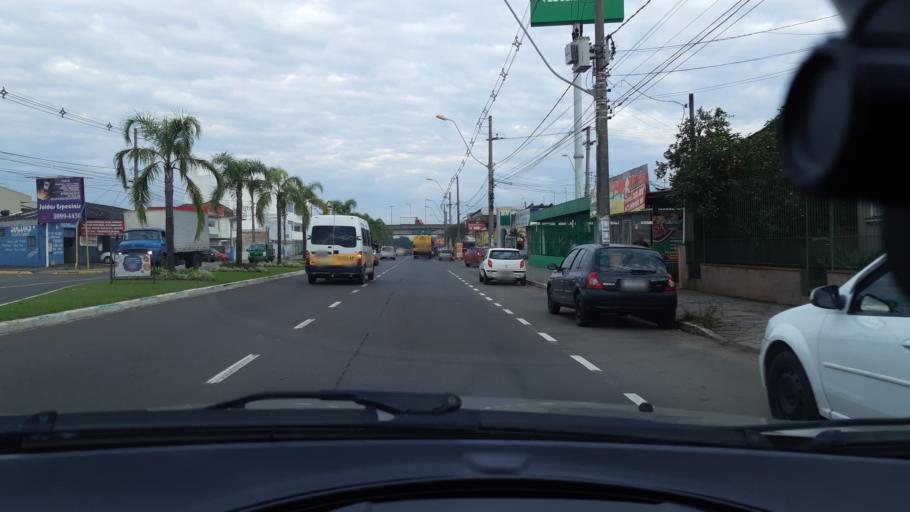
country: BR
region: Rio Grande do Sul
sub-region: Sao Leopoldo
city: Sao Leopoldo
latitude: -29.7720
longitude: -51.1518
